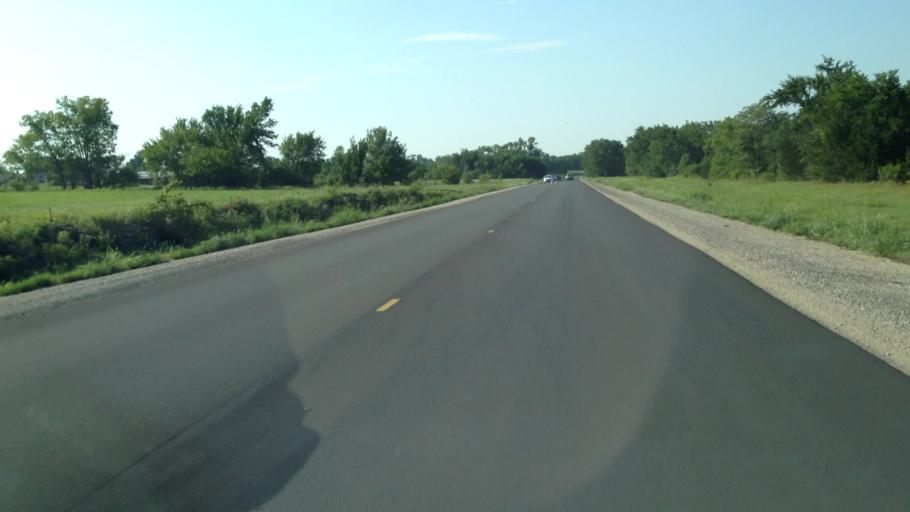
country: US
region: Kansas
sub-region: Anderson County
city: Garnett
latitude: 38.3130
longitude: -95.2496
